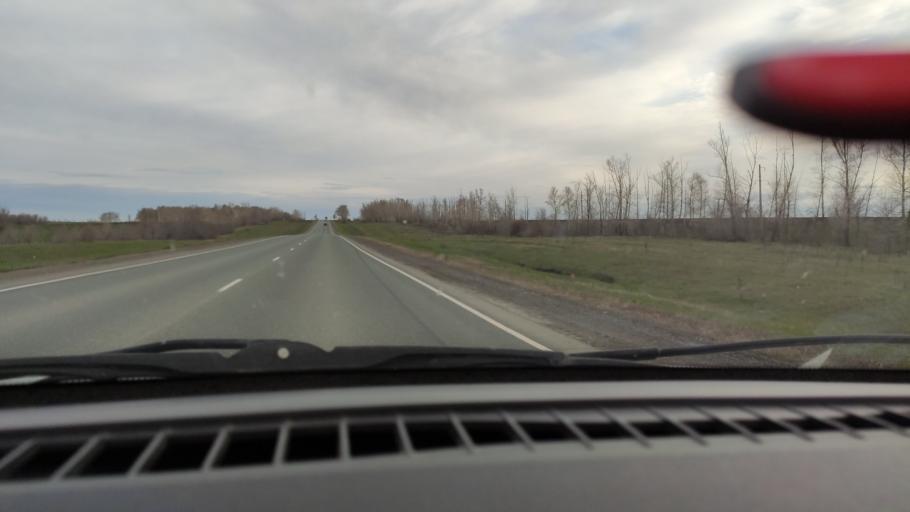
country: RU
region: Orenburg
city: Sakmara
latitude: 52.1515
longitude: 55.2863
